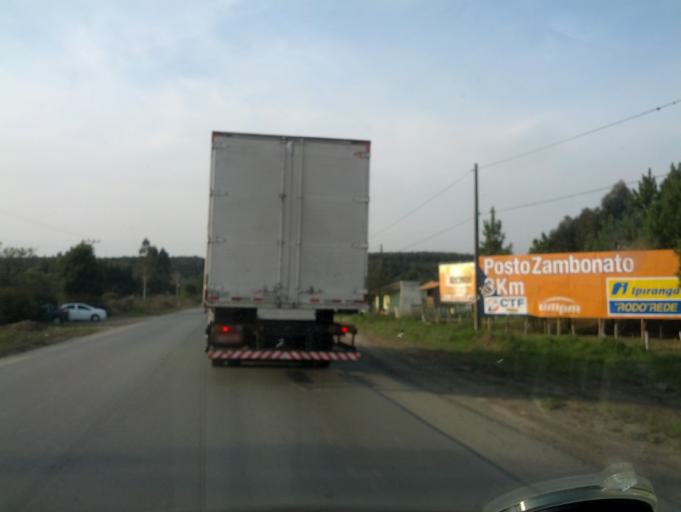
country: BR
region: Santa Catarina
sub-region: Otacilio Costa
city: Otacilio Costa
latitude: -27.5202
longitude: -50.1346
